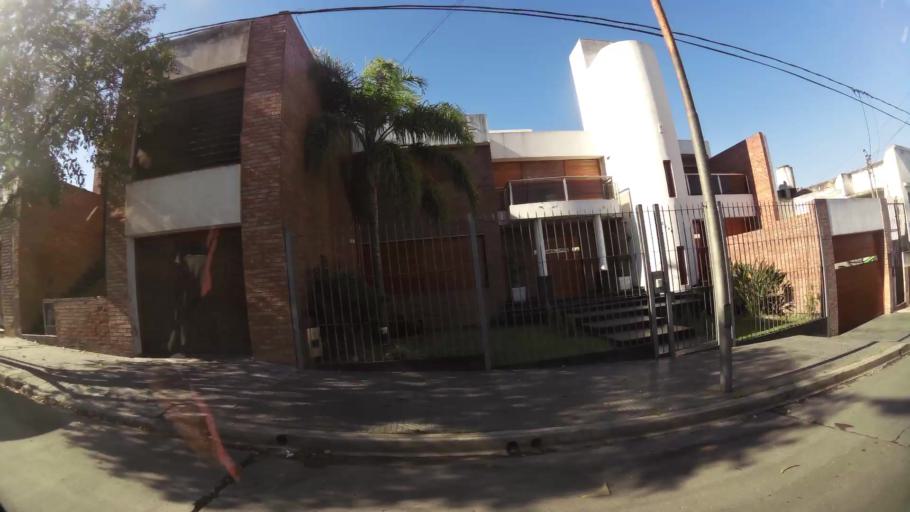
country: AR
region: Cordoba
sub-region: Departamento de Capital
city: Cordoba
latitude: -31.4264
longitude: -64.1394
